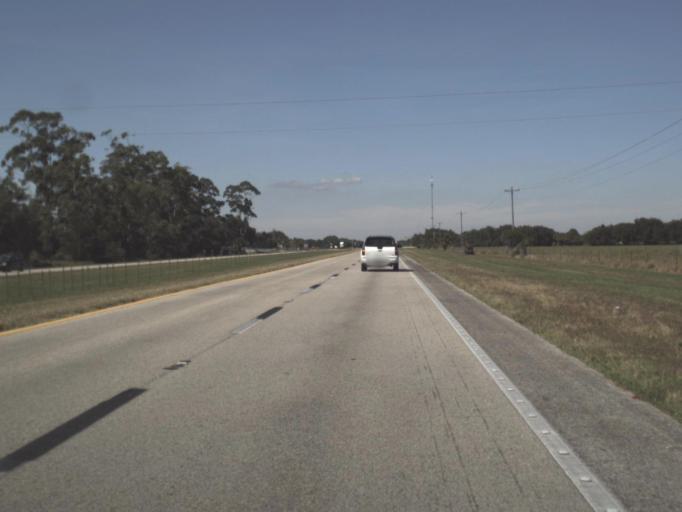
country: US
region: Florida
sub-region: Glades County
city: Moore Haven
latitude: 26.8588
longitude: -81.2100
